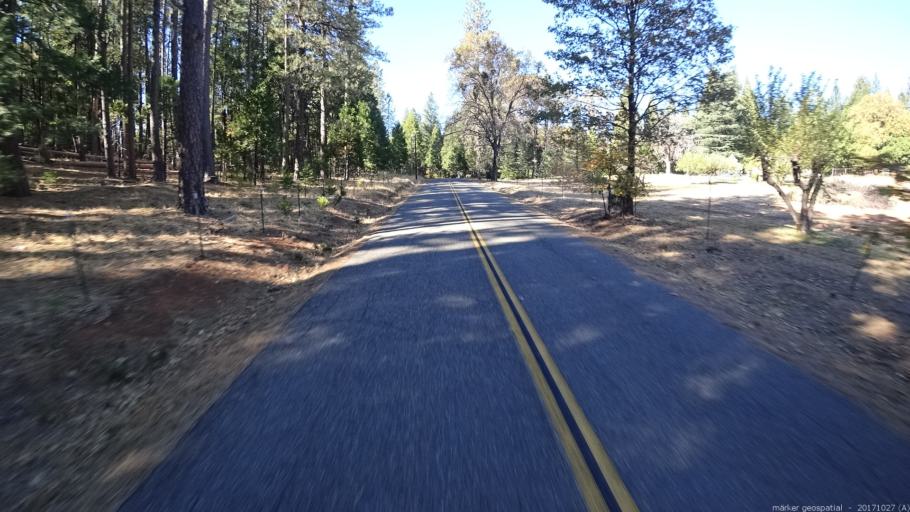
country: US
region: California
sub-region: Shasta County
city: Shingletown
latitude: 40.6880
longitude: -121.9099
